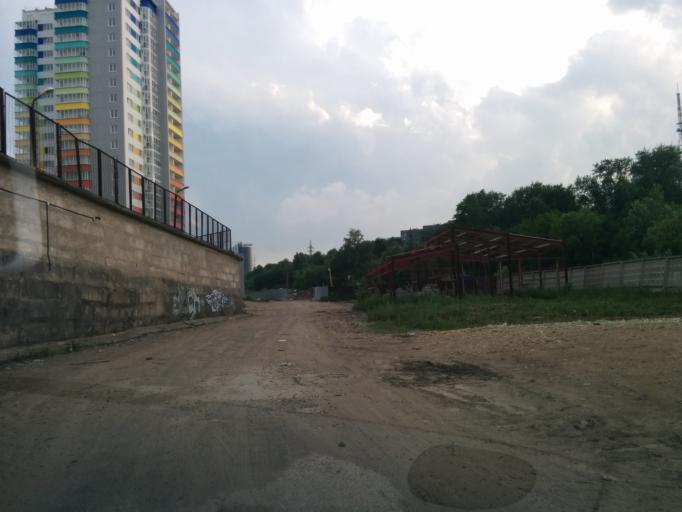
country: RU
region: Perm
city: Perm
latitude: 58.0118
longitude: 56.3043
